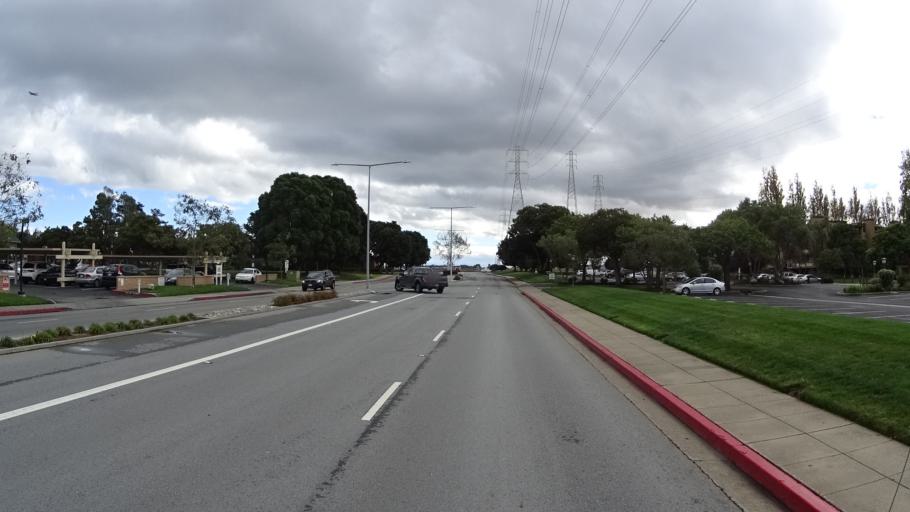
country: US
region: California
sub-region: San Mateo County
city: Foster City
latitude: 37.5525
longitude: -122.2535
